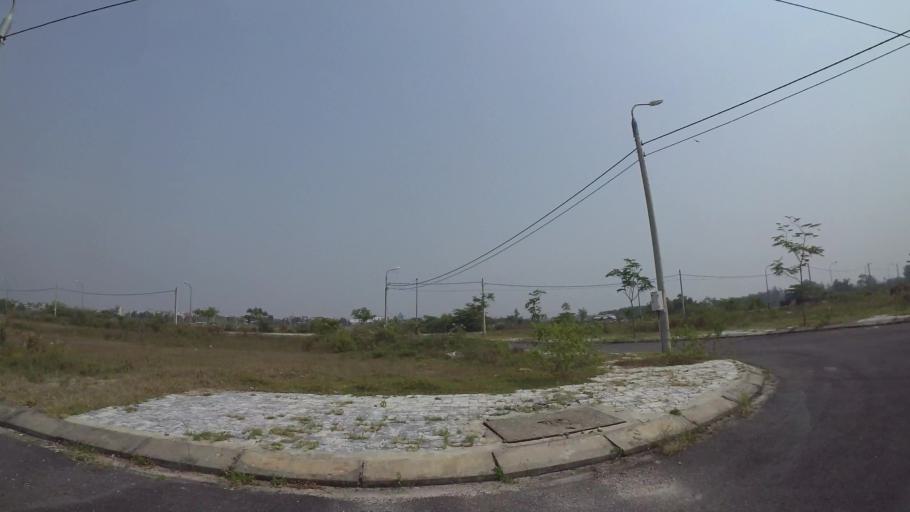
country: VN
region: Da Nang
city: Cam Le
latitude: 15.9709
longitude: 108.2136
